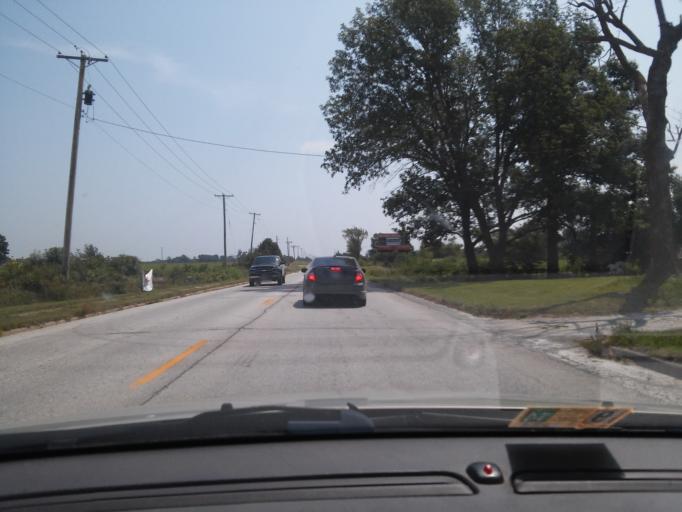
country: US
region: Missouri
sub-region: Pike County
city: Bowling Green
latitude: 39.3453
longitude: -91.3368
